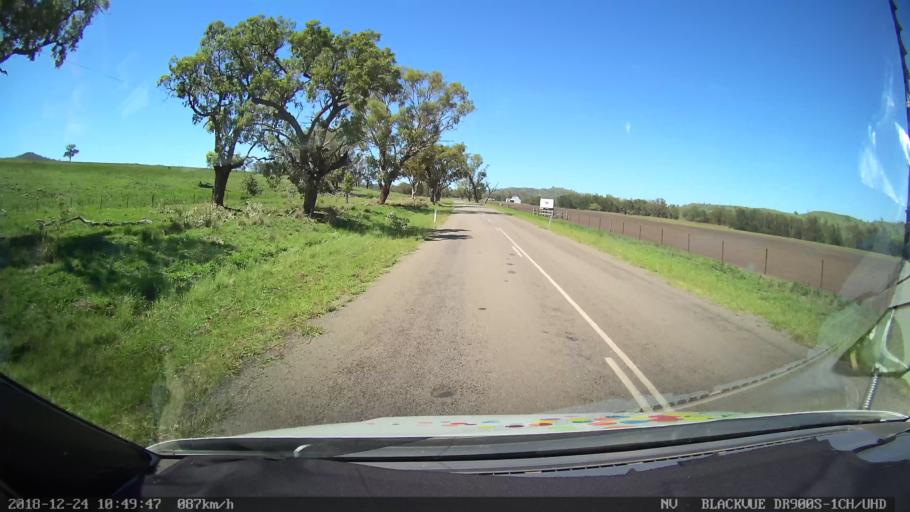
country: AU
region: New South Wales
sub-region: Upper Hunter Shire
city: Merriwa
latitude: -31.9518
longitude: 150.4258
